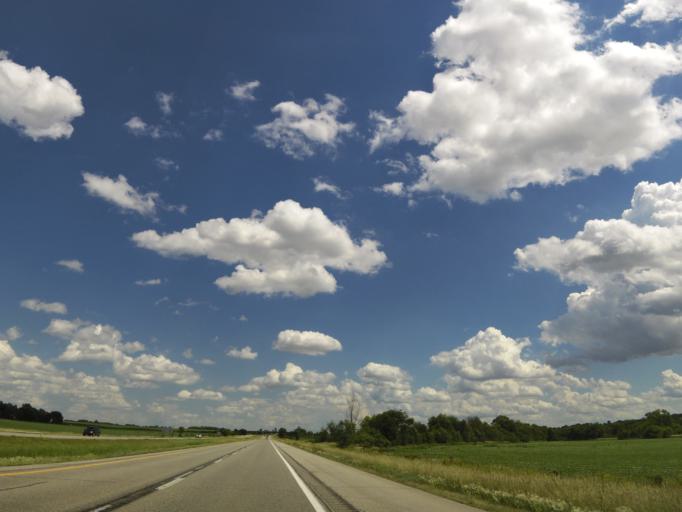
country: US
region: Iowa
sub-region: Linn County
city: Center Point
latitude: 42.1631
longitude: -91.7668
